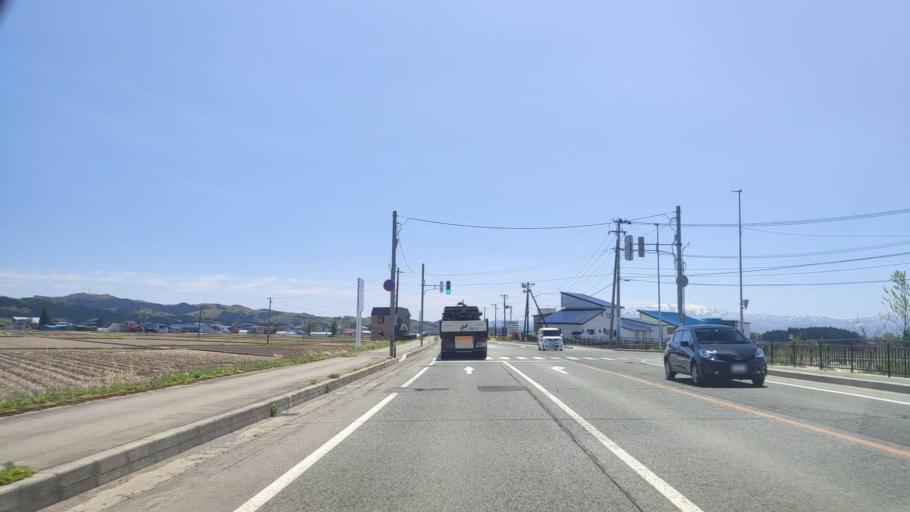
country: JP
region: Yamagata
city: Shinjo
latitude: 38.7948
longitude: 140.3185
